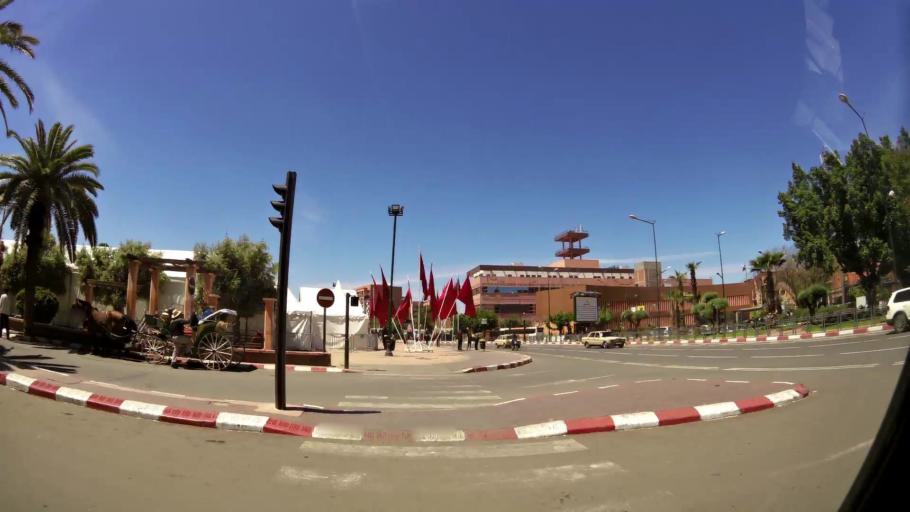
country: MA
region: Marrakech-Tensift-Al Haouz
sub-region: Marrakech
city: Marrakesh
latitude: 31.6319
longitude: -8.0083
